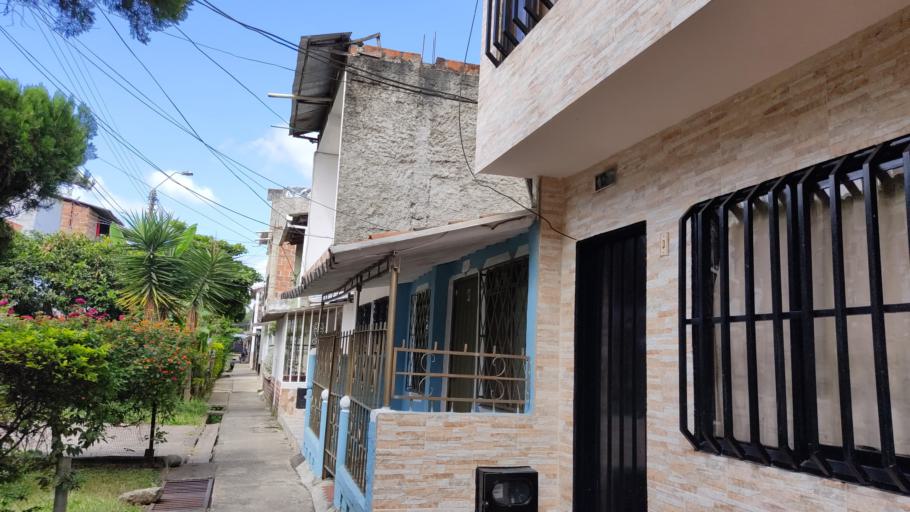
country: CO
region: Valle del Cauca
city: Jamundi
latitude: 3.2549
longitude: -76.5433
